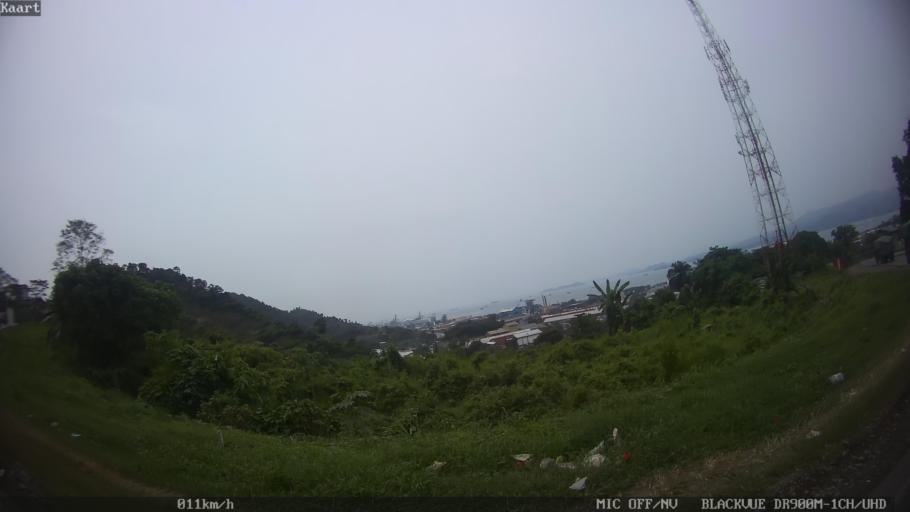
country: ID
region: Lampung
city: Panjang
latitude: -5.4413
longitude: 105.3133
